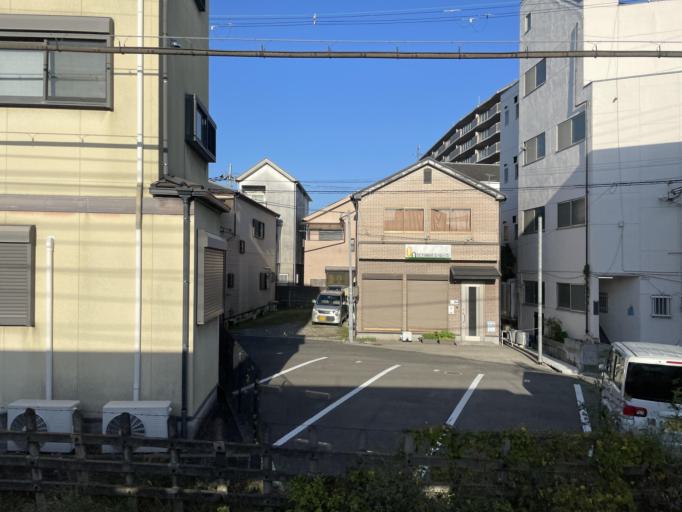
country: JP
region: Osaka
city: Kashihara
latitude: 34.5668
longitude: 135.6198
